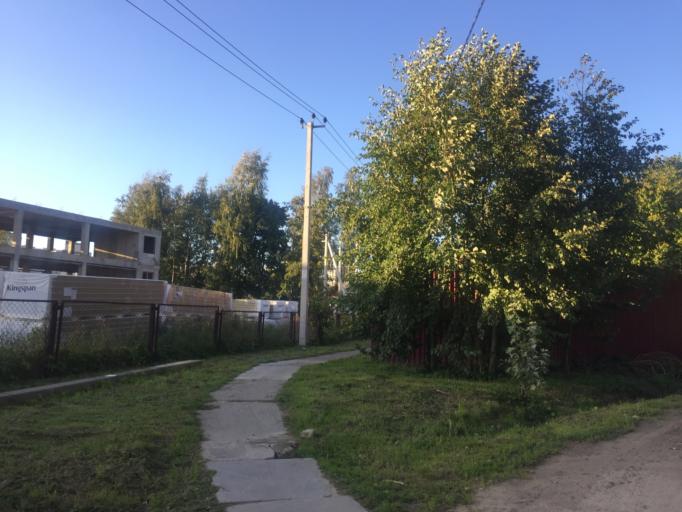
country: RU
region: Leningrad
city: Murino
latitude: 60.0443
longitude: 30.4421
